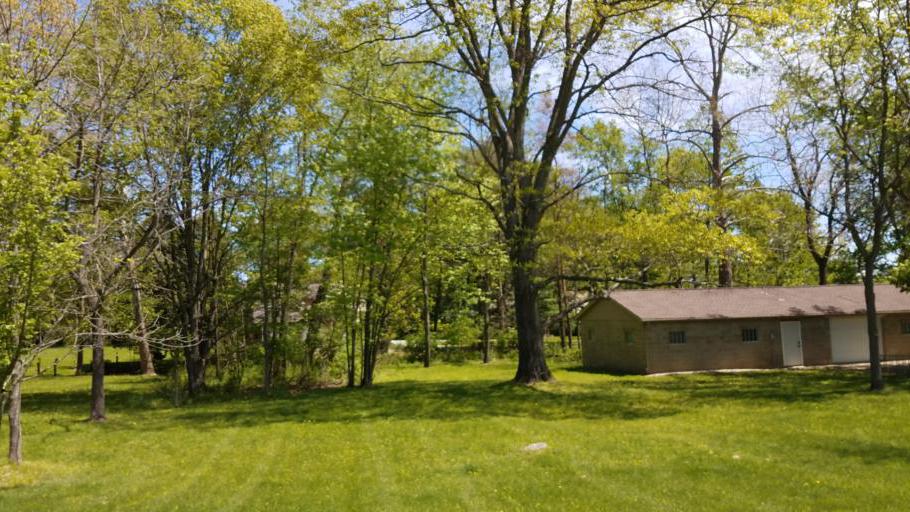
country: US
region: Ohio
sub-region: Knox County
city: Gambier
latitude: 40.3766
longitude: -82.3879
